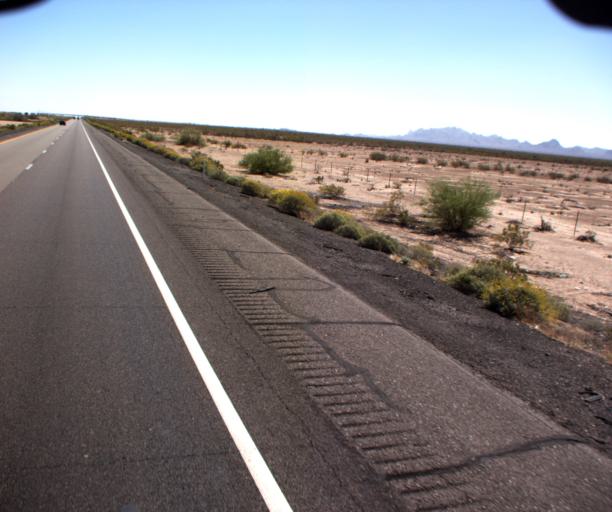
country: US
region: Arizona
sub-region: La Paz County
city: Salome
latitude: 33.5984
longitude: -113.5501
